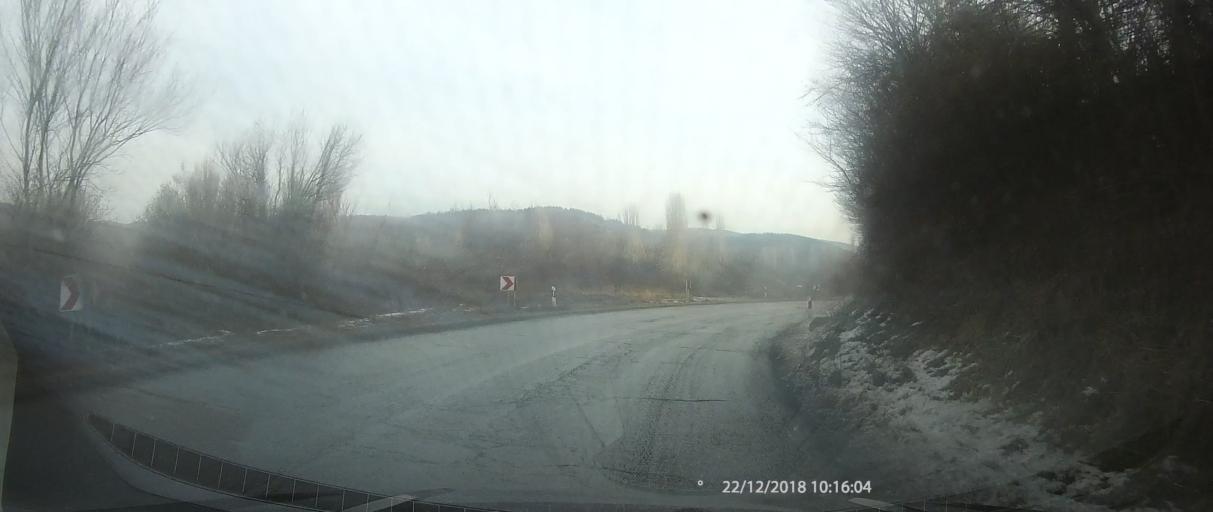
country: MK
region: Kriva Palanka
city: Kriva Palanka
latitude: 42.1788
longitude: 22.2613
